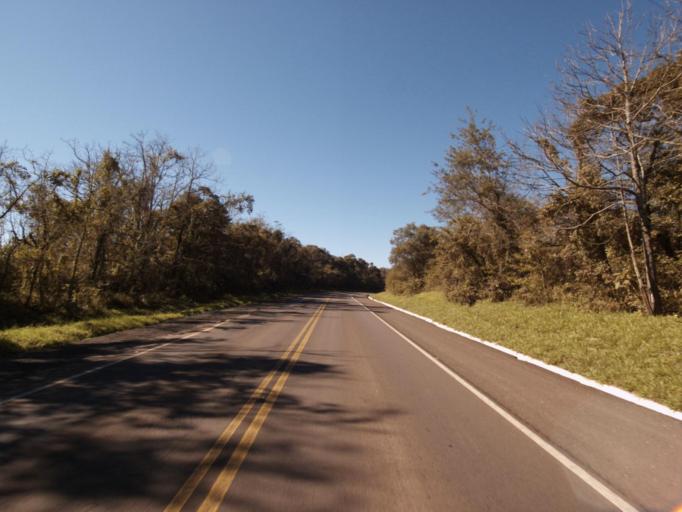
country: BR
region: Rio Grande do Sul
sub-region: Frederico Westphalen
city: Frederico Westphalen
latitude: -26.7974
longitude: -53.3234
